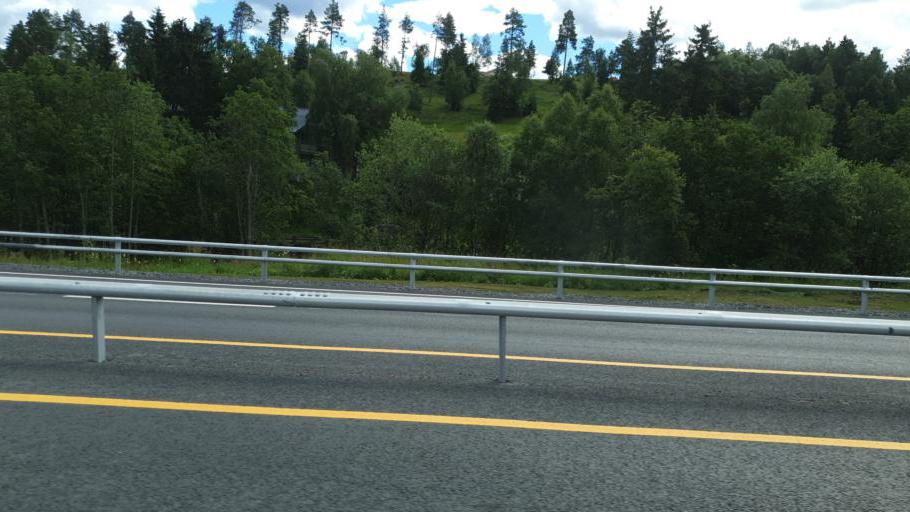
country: NO
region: Sor-Trondelag
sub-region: Midtre Gauldal
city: Storen
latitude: 62.9372
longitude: 10.1881
